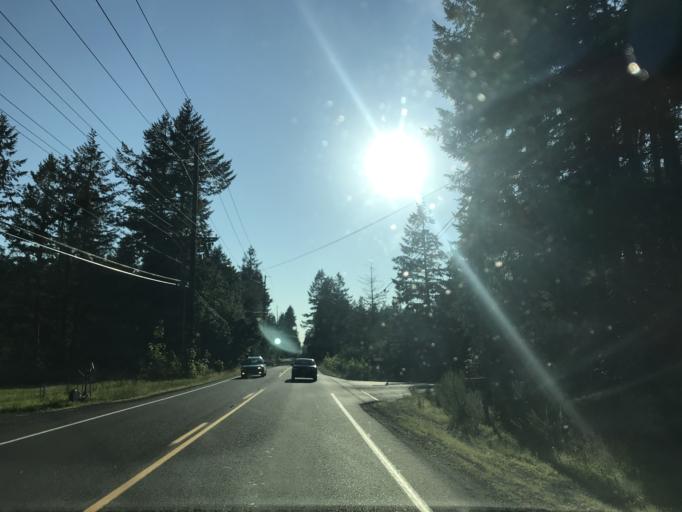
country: US
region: Washington
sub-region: King County
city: Maple Valley
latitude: 47.3870
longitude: -122.0716
